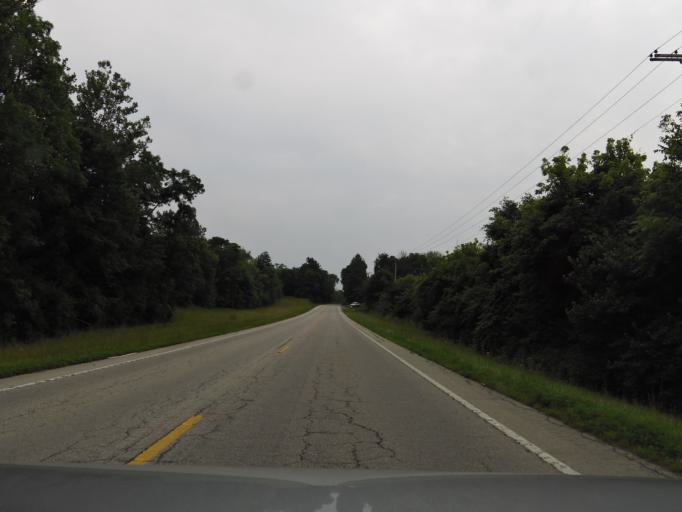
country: US
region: Ohio
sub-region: Clinton County
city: Wilmington
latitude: 39.3834
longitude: -83.8598
